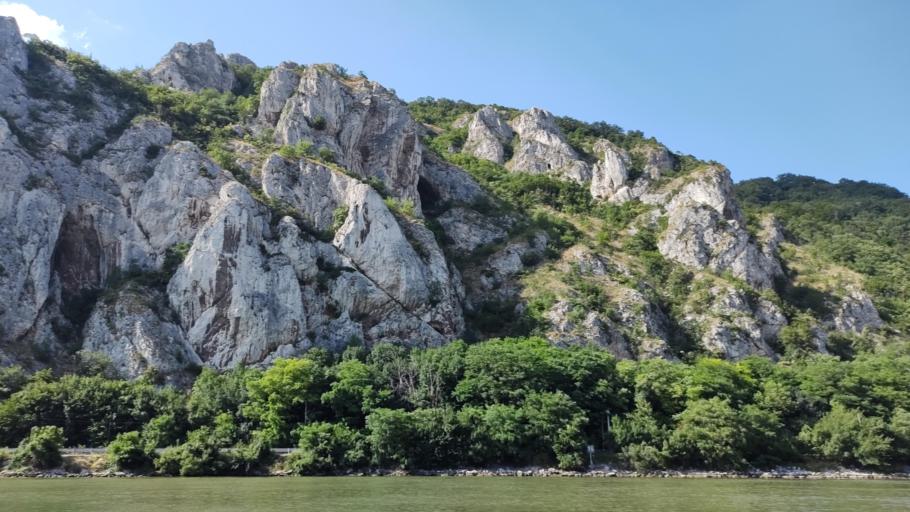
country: RO
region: Caras-Severin
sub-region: Comuna Pescari
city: Coronini
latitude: 44.6542
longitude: 21.7268
